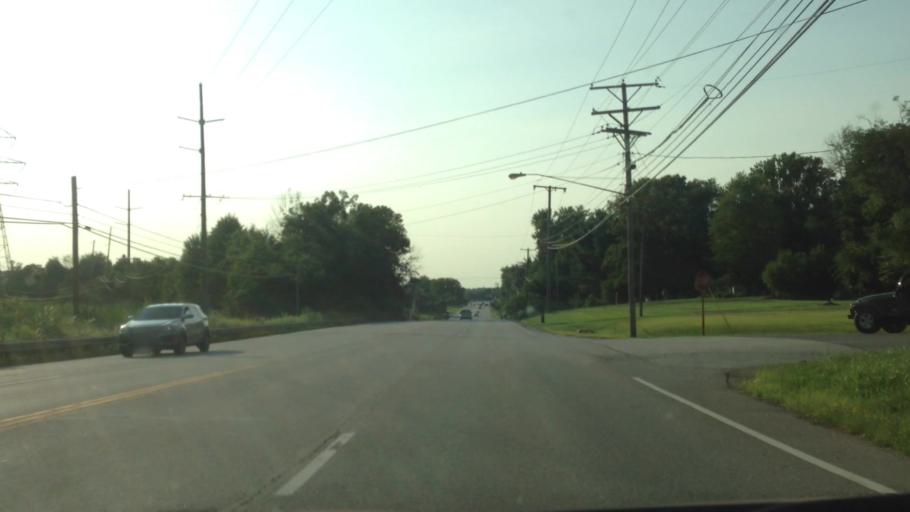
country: US
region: Ohio
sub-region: Summit County
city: Fairlawn
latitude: 41.1446
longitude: -81.6209
